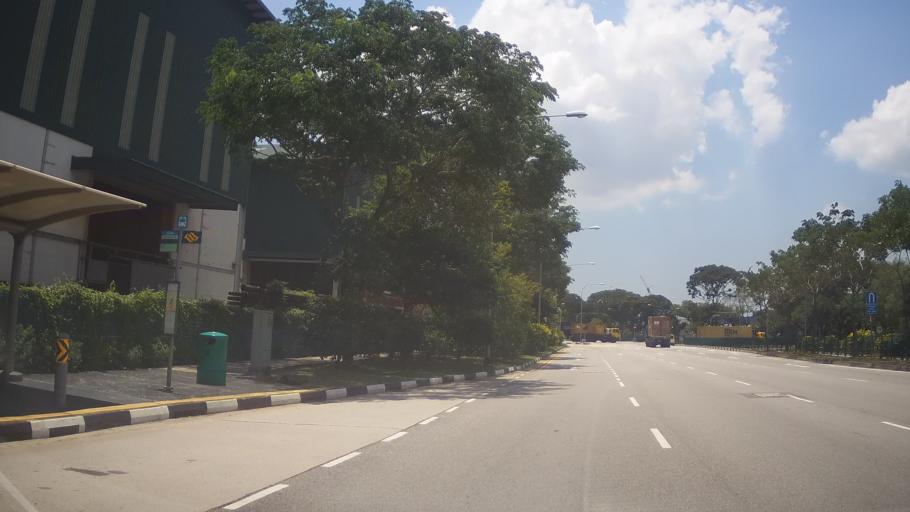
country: SG
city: Singapore
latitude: 1.3112
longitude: 103.6788
